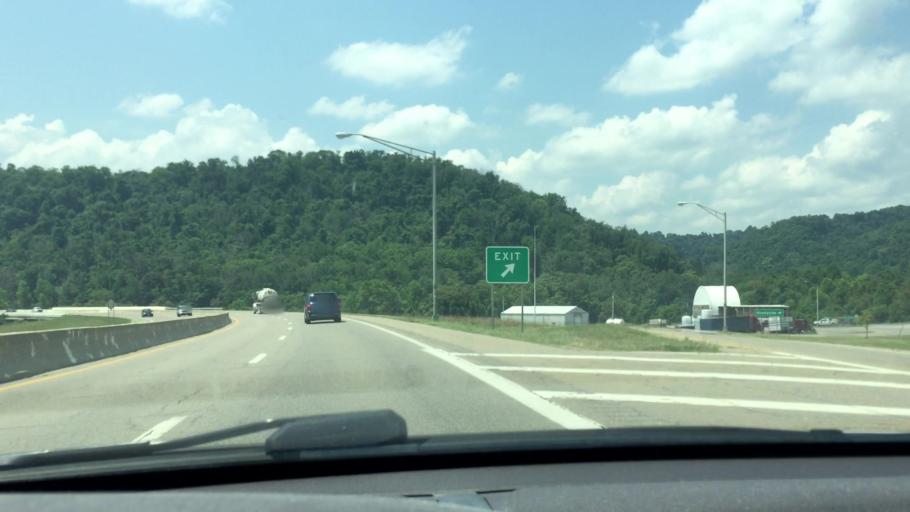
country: US
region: Ohio
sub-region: Belmont County
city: Shadyside
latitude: 39.9621
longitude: -80.7578
